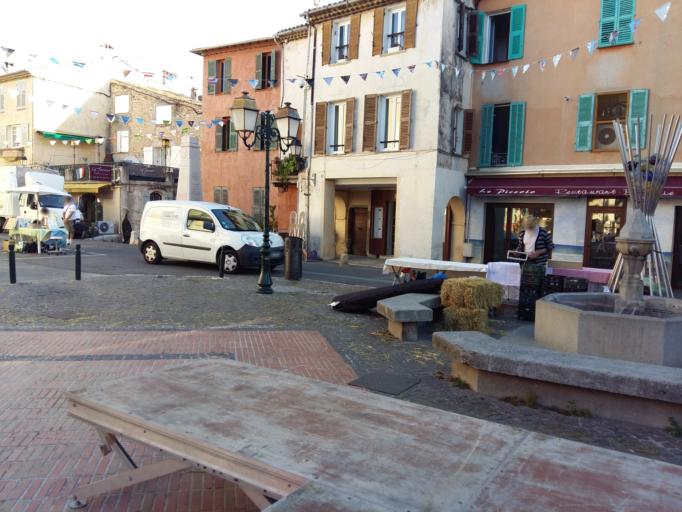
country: FR
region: Provence-Alpes-Cote d'Azur
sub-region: Departement des Alpes-Maritimes
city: Biot
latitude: 43.6275
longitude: 7.0976
